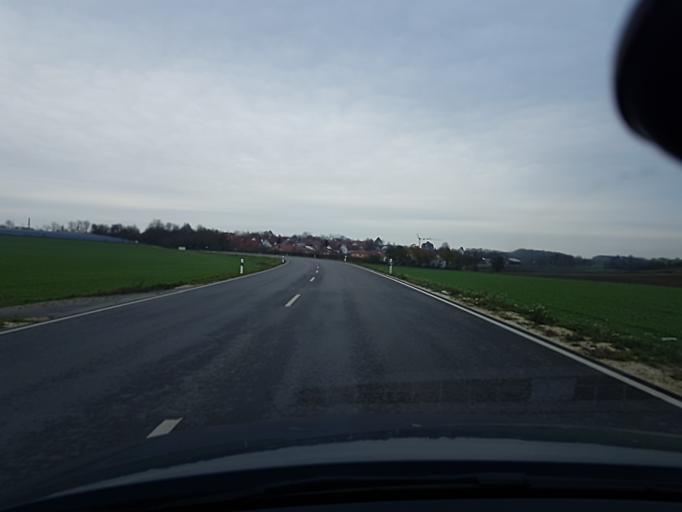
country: DE
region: Bavaria
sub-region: Upper Palatinate
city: Schierling
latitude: 48.8305
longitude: 12.1796
